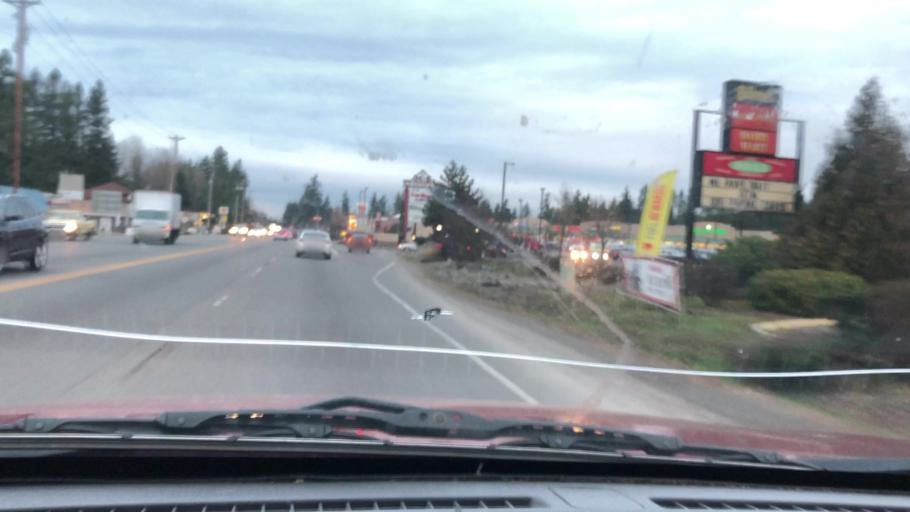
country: US
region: Washington
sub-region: Pierce County
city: Elk Plain
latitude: 47.0535
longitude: -122.3981
